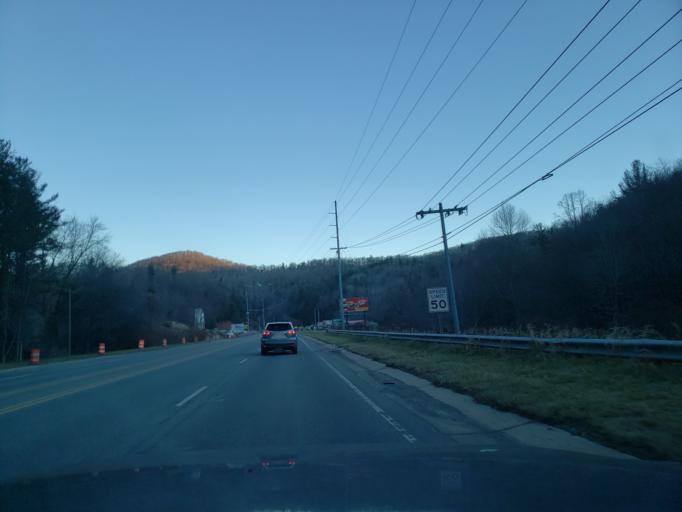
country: US
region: North Carolina
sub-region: Watauga County
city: Boone
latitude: 36.1755
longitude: -81.6484
